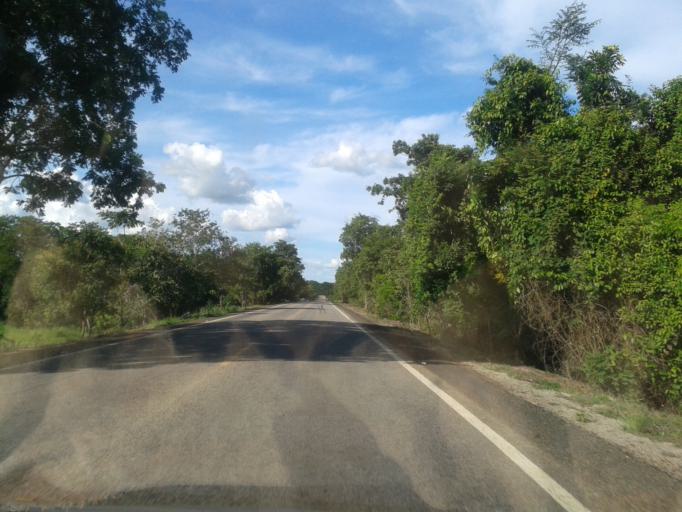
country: BR
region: Goias
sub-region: Mozarlandia
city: Mozarlandia
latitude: -14.5795
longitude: -50.5039
